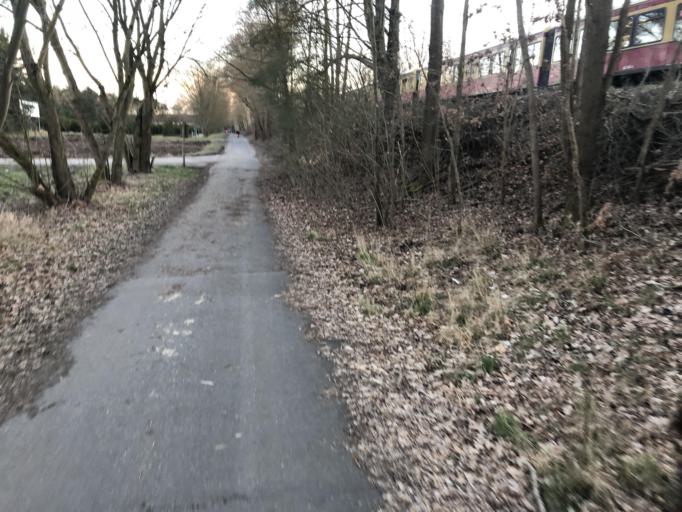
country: DE
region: Berlin
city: Frohnau
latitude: 52.6514
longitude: 13.2857
